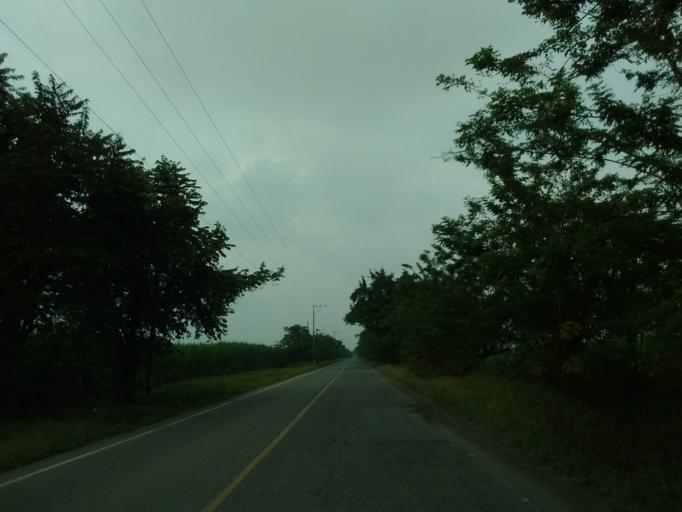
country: CO
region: Cauca
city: Padilla
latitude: 3.2274
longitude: -76.3412
